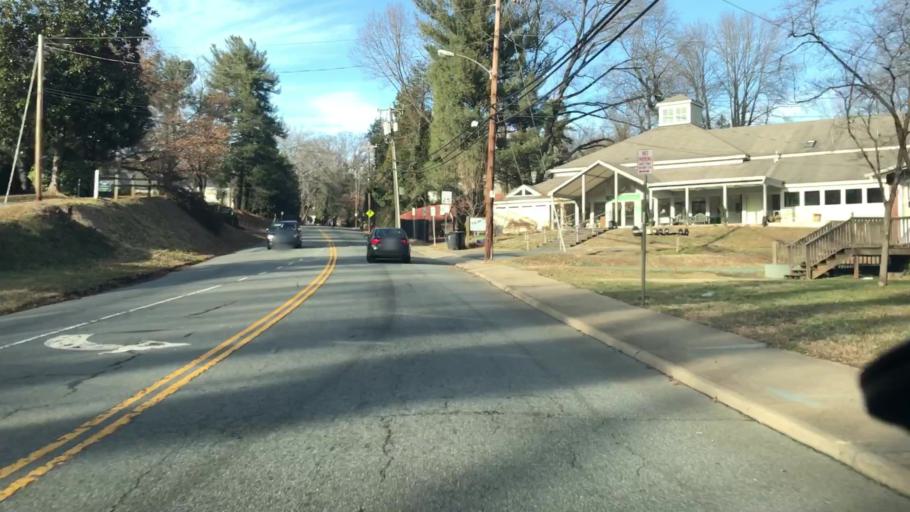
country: US
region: Virginia
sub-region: City of Charlottesville
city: Charlottesville
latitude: 38.0420
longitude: -78.4922
